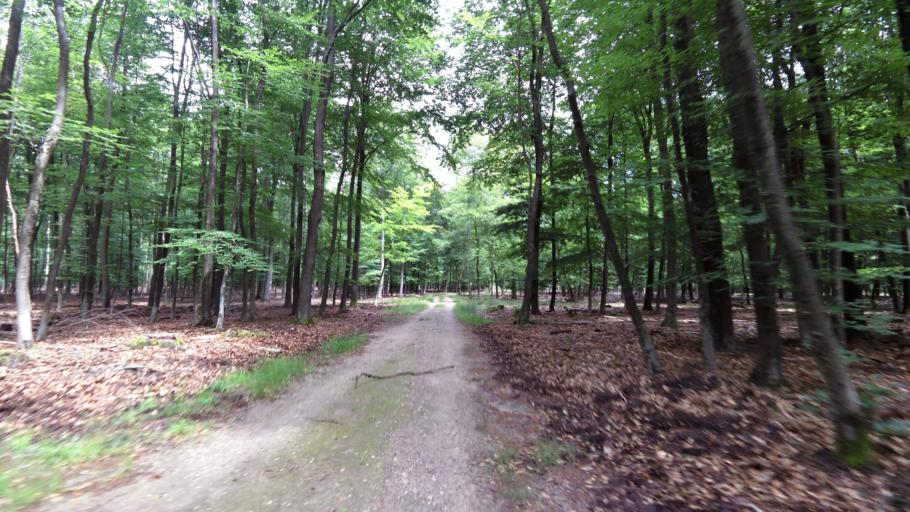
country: NL
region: Gelderland
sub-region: Gemeente Apeldoorn
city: Apeldoorn
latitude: 52.2284
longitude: 5.8927
